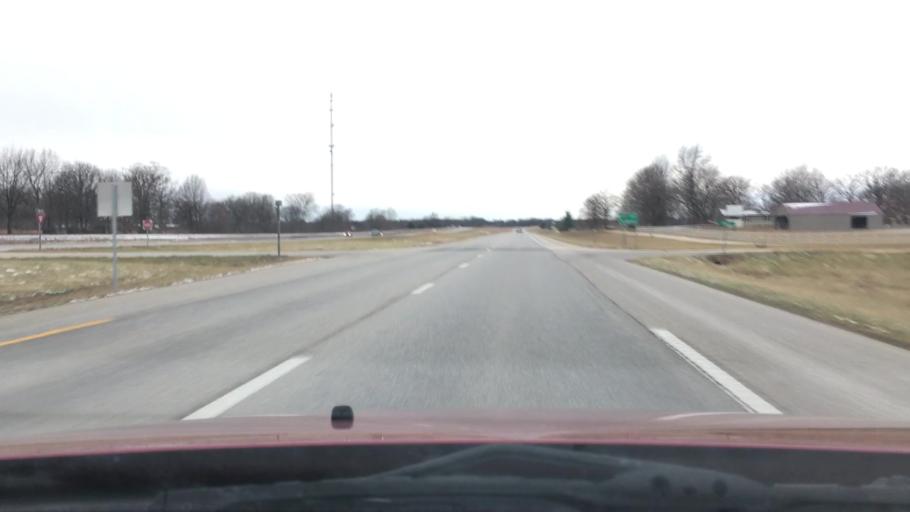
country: US
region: Missouri
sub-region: Webster County
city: Seymour
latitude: 37.1694
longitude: -92.8129
